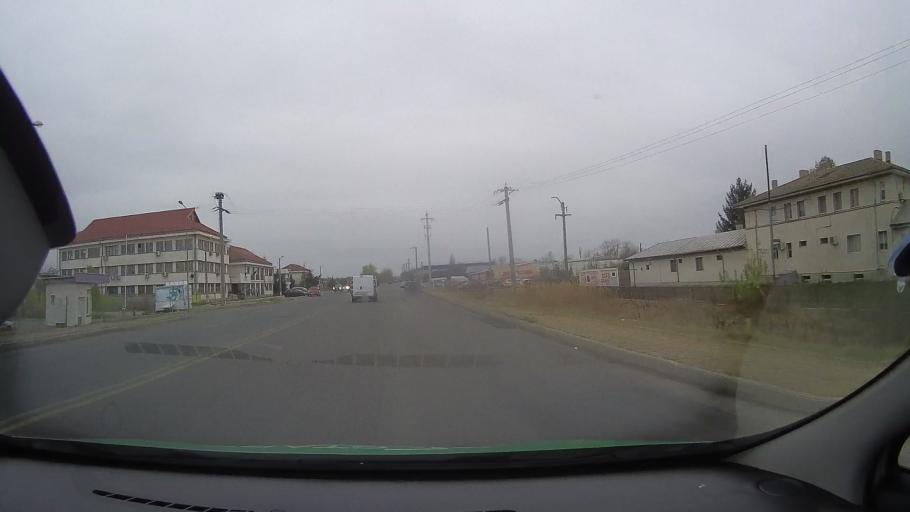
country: RO
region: Ialomita
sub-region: Comuna Slobozia
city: Slobozia
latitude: 44.5797
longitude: 27.3875
